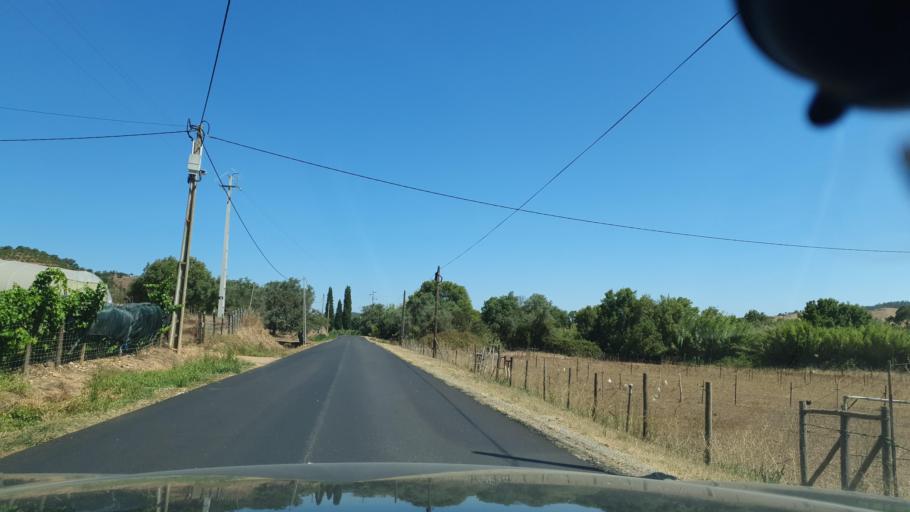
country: PT
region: Faro
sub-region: Monchique
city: Monchique
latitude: 37.4642
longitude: -8.4878
